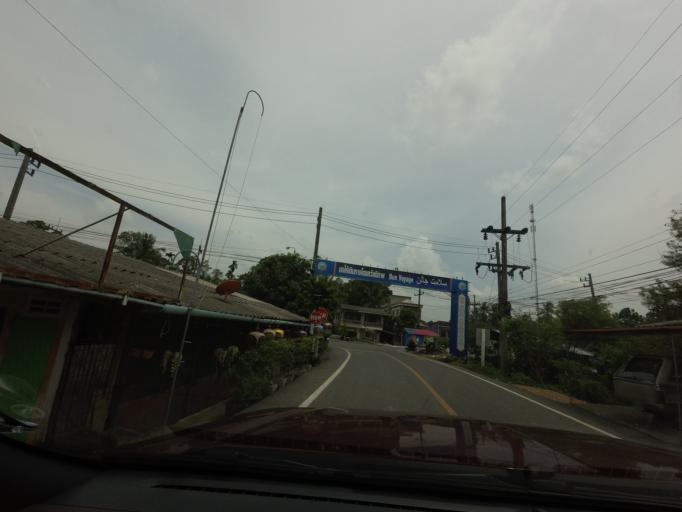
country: TH
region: Pattani
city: Yarang
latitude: 6.7126
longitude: 101.2908
